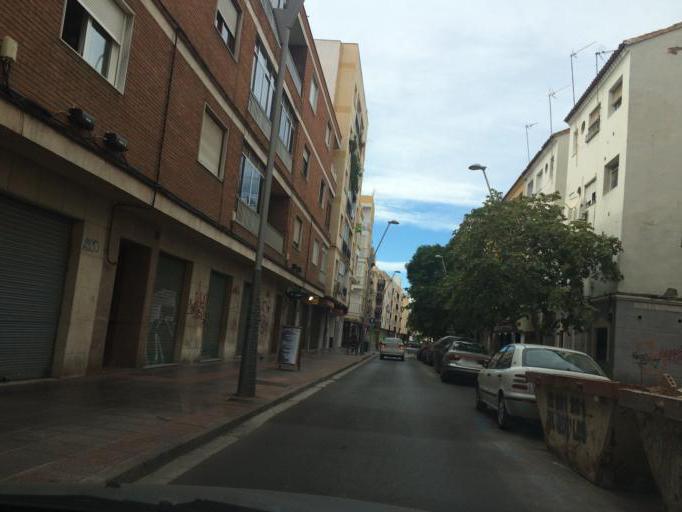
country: ES
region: Andalusia
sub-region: Provincia de Almeria
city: Almeria
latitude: 36.8427
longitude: -2.4545
